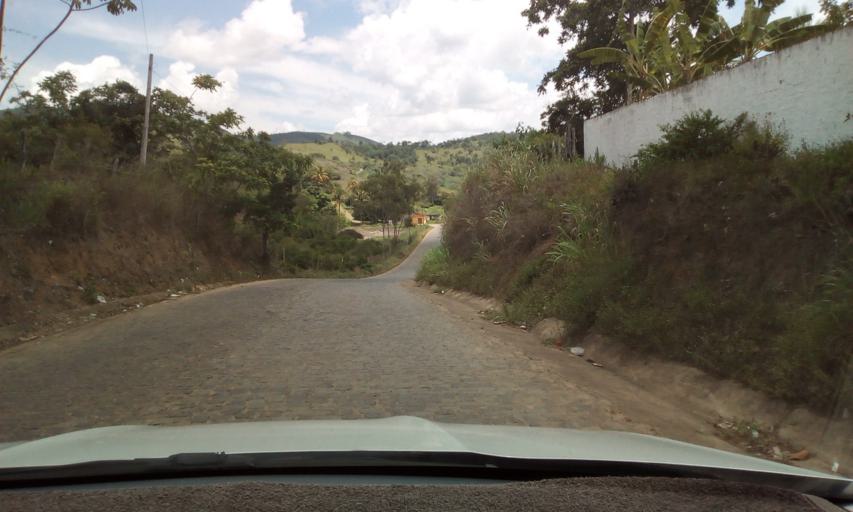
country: BR
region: Pernambuco
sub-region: Bonito
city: Bonito
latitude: -8.4793
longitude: -35.7291
